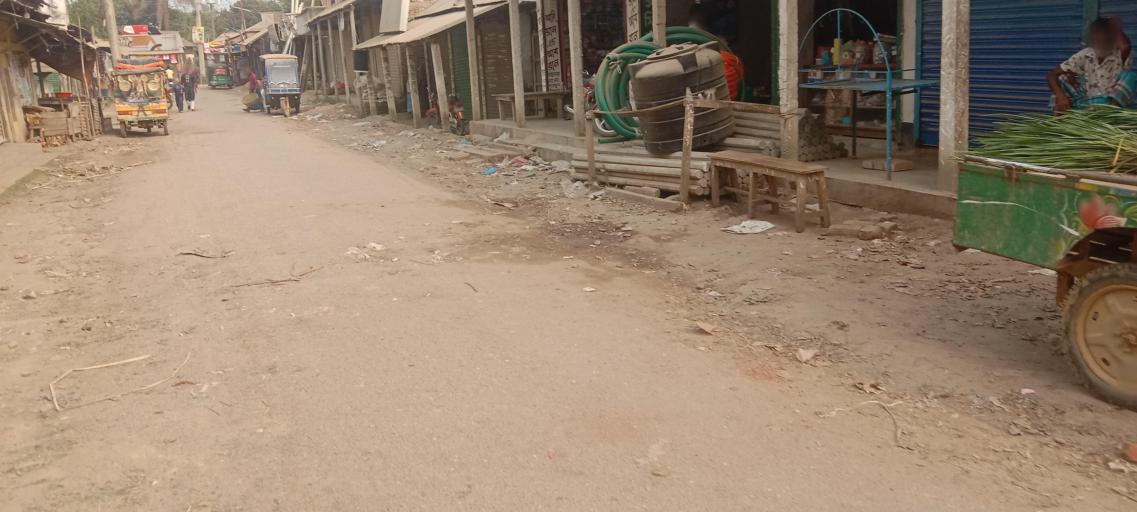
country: BD
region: Dhaka
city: Gafargaon
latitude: 24.3837
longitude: 90.4728
